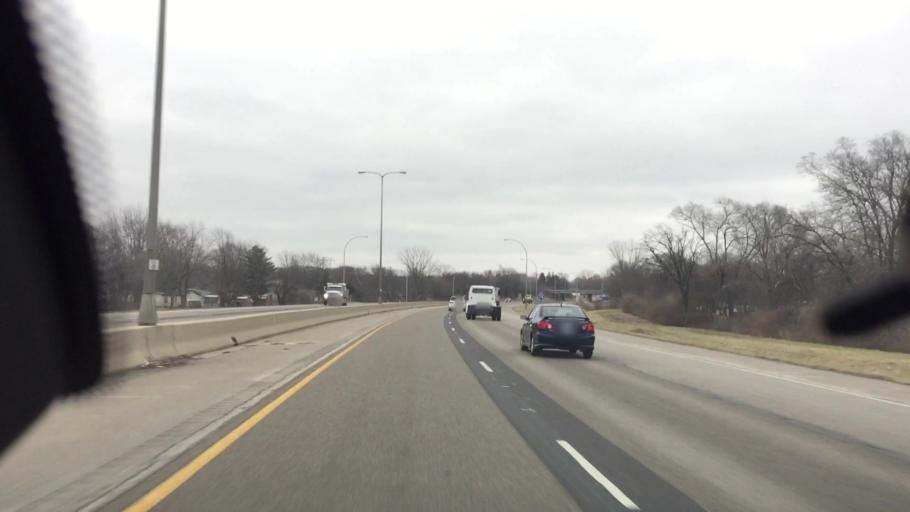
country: US
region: Illinois
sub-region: Champaign County
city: Urbana
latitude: 40.1319
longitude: -88.1901
